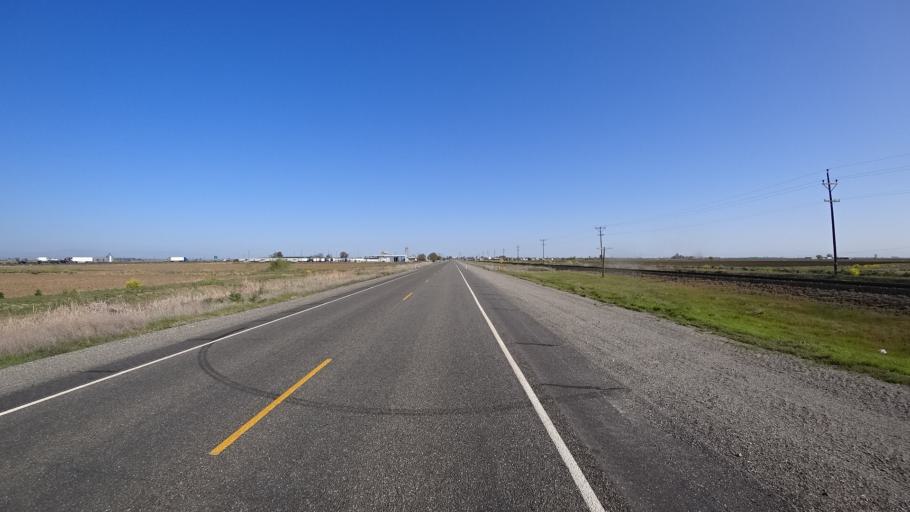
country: US
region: California
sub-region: Glenn County
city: Willows
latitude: 39.4882
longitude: -122.1932
